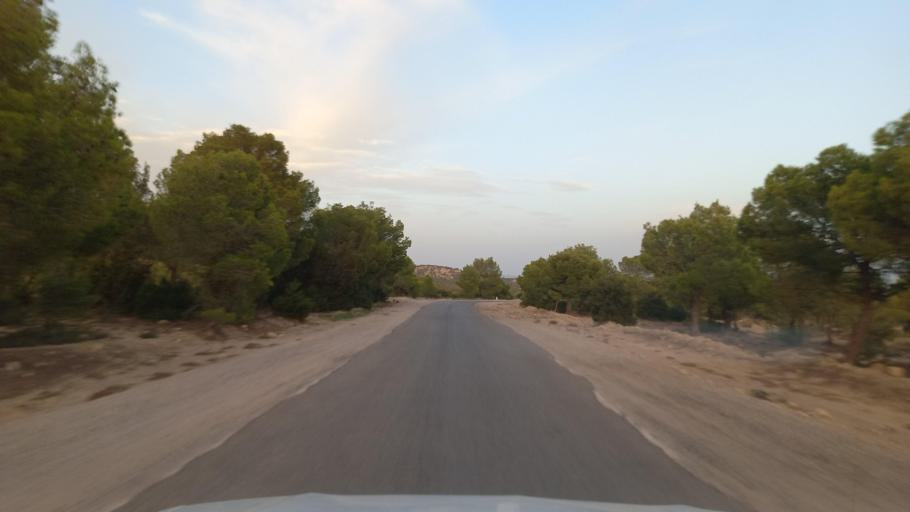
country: TN
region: Al Qasrayn
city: Sbiba
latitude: 35.4132
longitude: 8.9352
